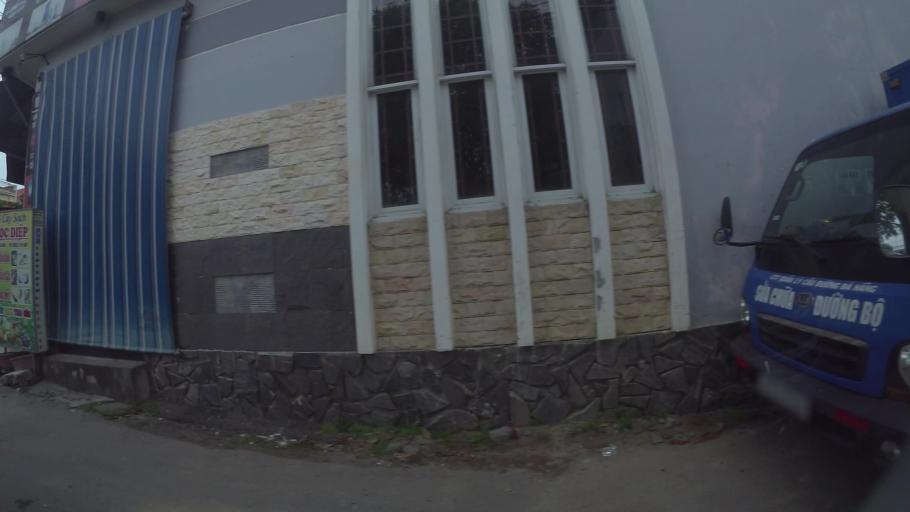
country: VN
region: Da Nang
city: Thanh Khe
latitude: 16.0497
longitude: 108.1807
